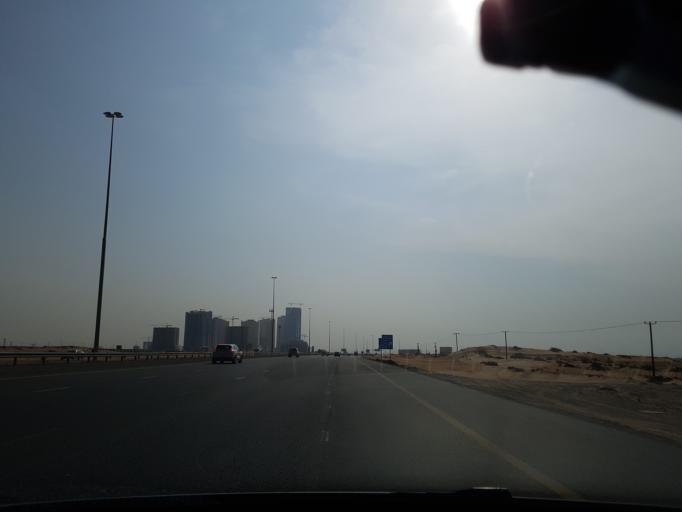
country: AE
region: Ajman
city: Ajman
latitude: 25.4078
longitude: 55.5831
